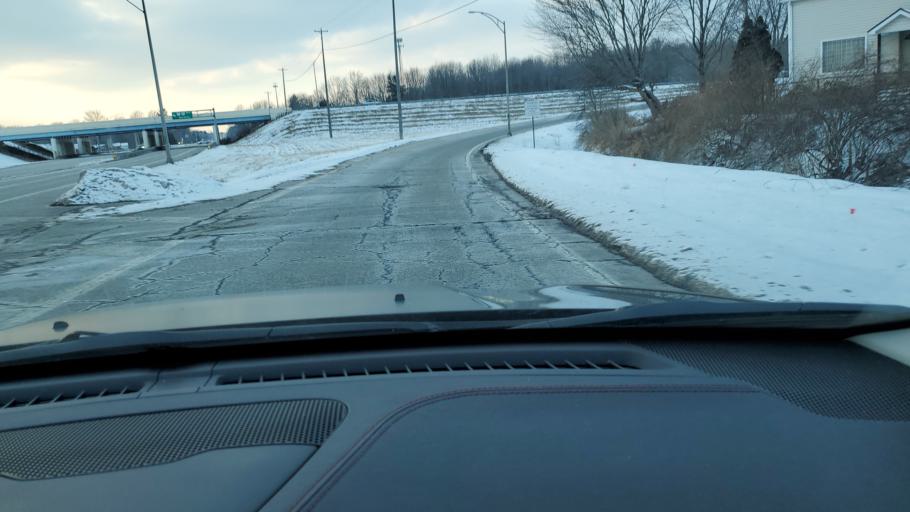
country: US
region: Ohio
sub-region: Trumbull County
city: Leavittsburg
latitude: 41.2625
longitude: -80.8745
